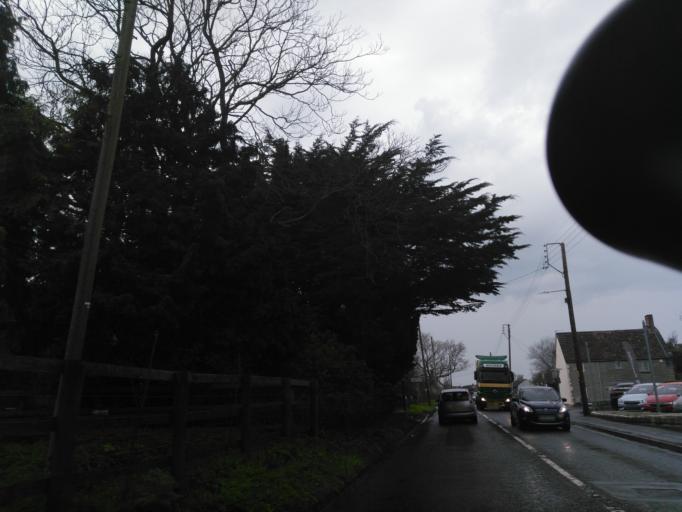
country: GB
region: England
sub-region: Somerset
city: Street
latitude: 51.1239
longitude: -2.7638
